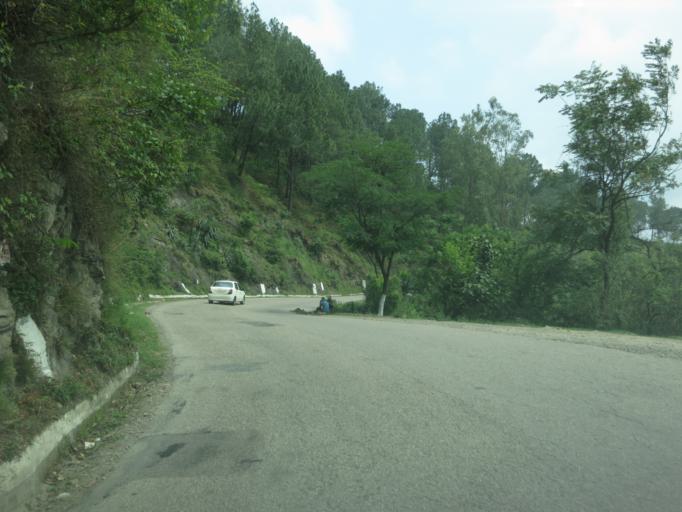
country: IN
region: Himachal Pradesh
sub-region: Bilaspur
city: Bilaspur
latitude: 31.2582
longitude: 76.8695
